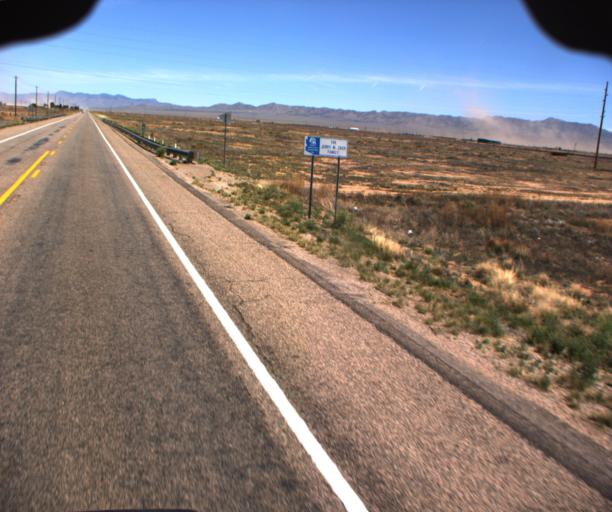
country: US
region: Arizona
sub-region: Mohave County
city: New Kingman-Butler
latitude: 35.2774
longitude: -113.9533
